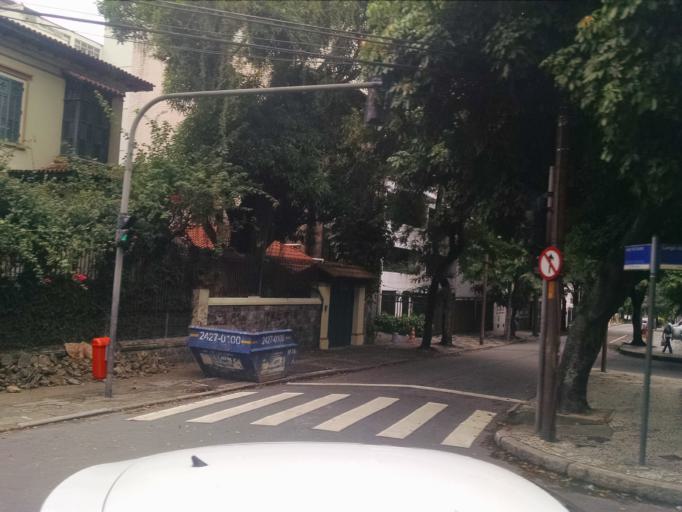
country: BR
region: Rio de Janeiro
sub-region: Rio De Janeiro
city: Rio de Janeiro
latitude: -22.9525
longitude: -43.1963
